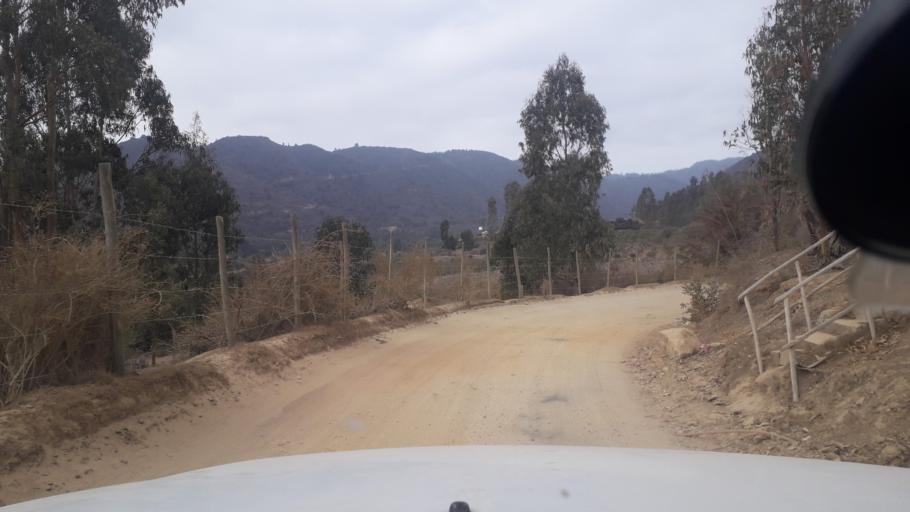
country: CL
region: Valparaiso
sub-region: Provincia de Valparaiso
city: Valparaiso
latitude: -33.1150
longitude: -71.6479
